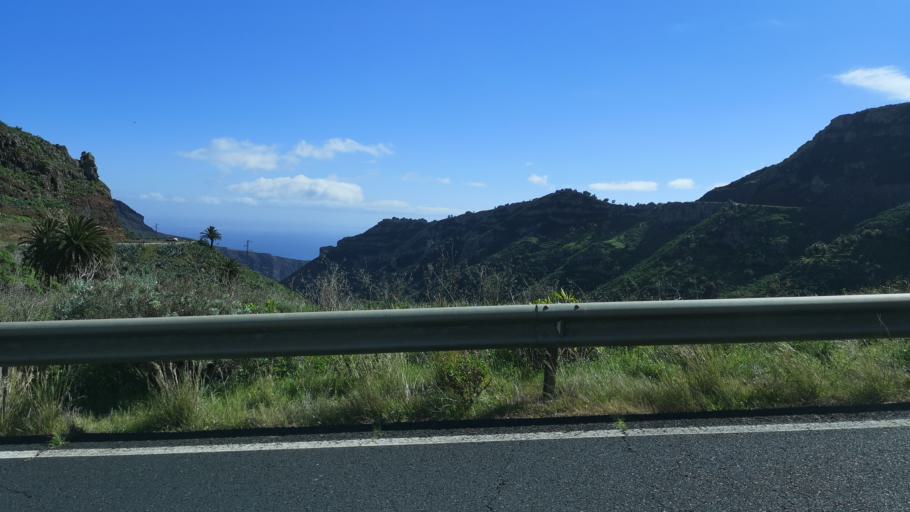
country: ES
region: Canary Islands
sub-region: Provincia de Santa Cruz de Tenerife
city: Alajero
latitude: 28.0961
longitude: -17.2009
